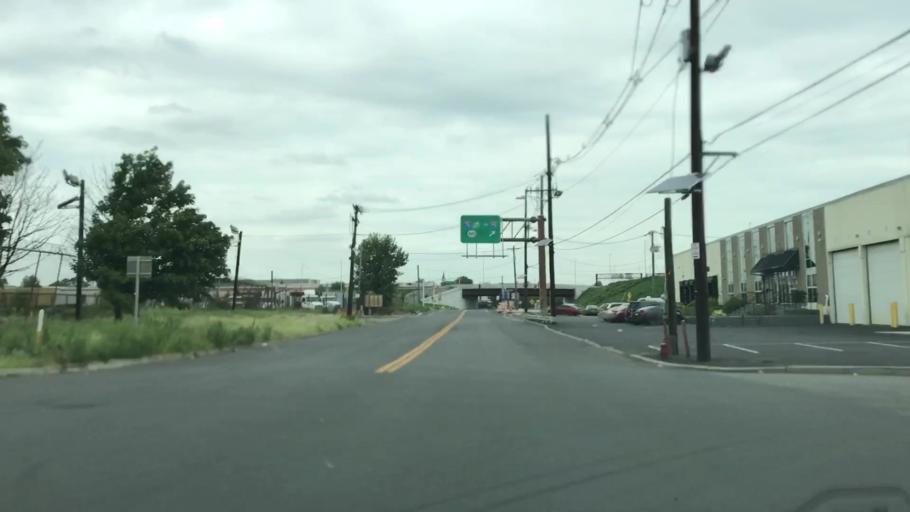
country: US
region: New Jersey
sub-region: Hudson County
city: Bayonne
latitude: 40.6777
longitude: -74.0944
